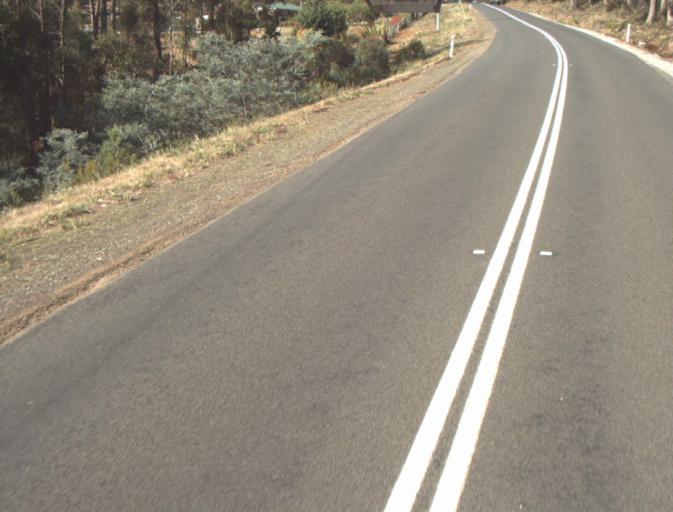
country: AU
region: Tasmania
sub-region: Launceston
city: Mayfield
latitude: -41.3379
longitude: 147.1643
